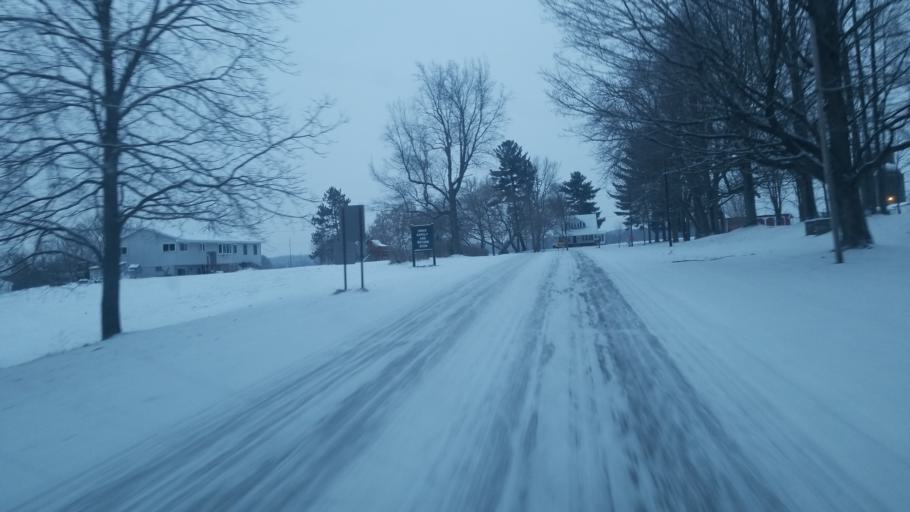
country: US
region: Michigan
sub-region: Osceola County
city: Reed City
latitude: 43.8448
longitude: -85.4445
